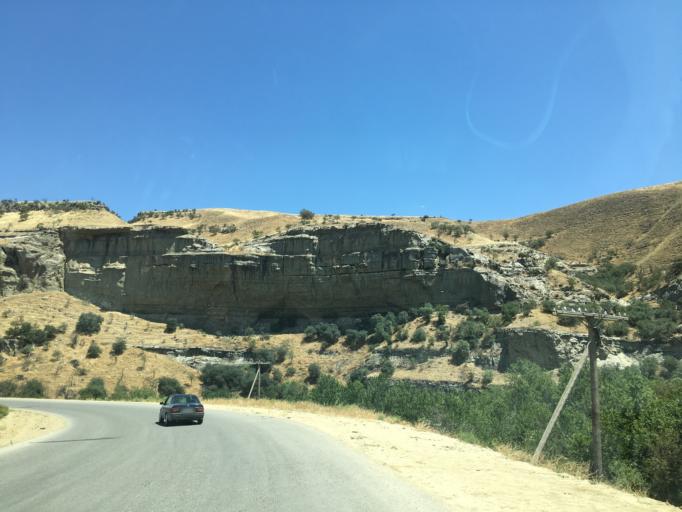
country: TM
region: Balkan
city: Magtymguly
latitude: 38.4170
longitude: 56.6790
